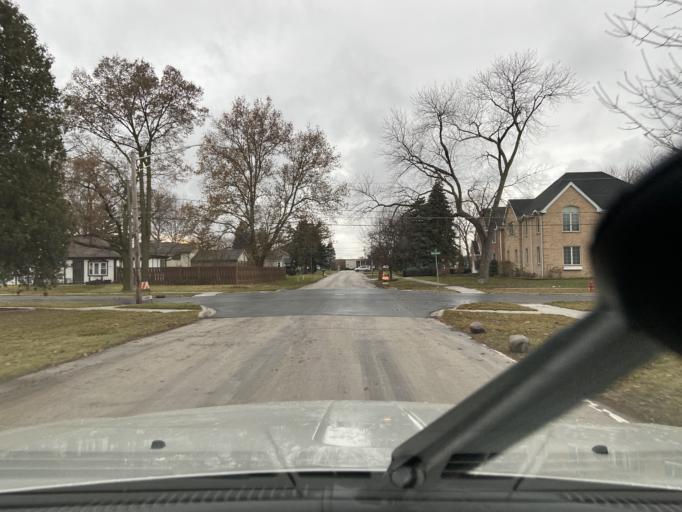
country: US
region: Illinois
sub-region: Cook County
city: Rosemont
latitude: 42.0128
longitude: -87.9058
